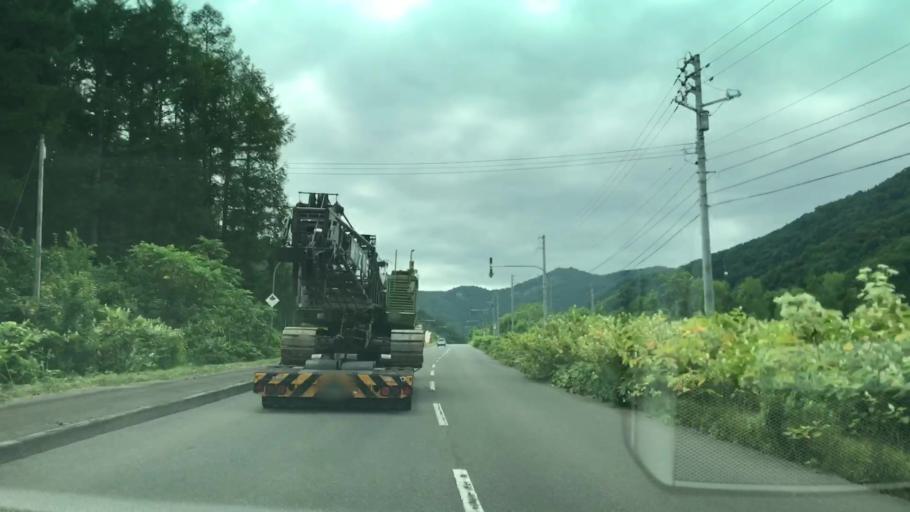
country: JP
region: Hokkaido
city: Yoichi
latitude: 43.0301
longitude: 140.8657
